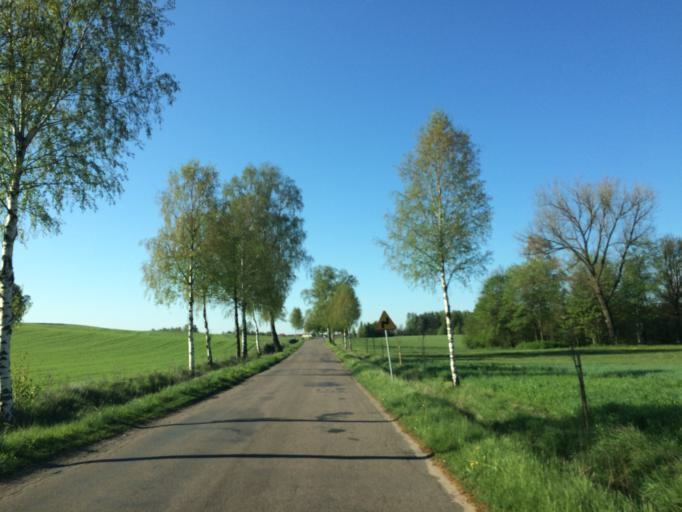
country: PL
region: Warmian-Masurian Voivodeship
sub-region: Powiat dzialdowski
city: Rybno
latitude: 53.4008
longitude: 19.9348
